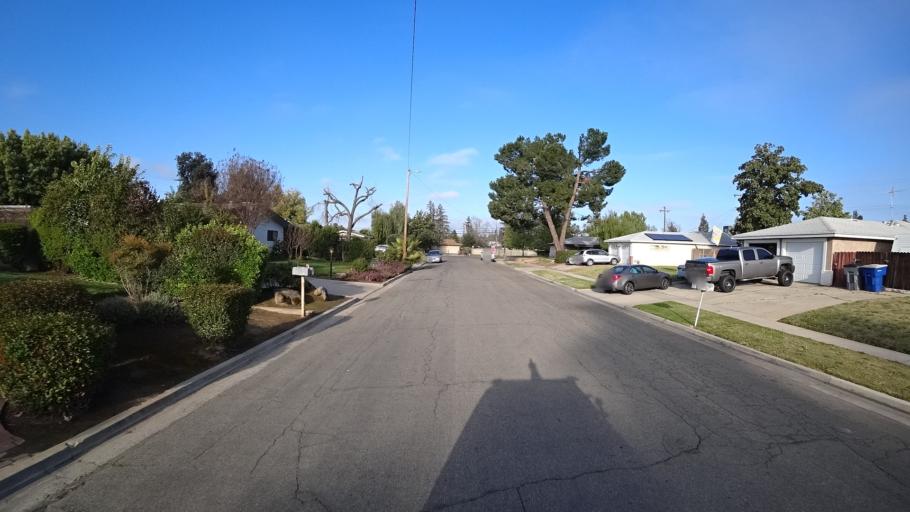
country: US
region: California
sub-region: Fresno County
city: Fresno
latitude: 36.8211
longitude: -119.7939
